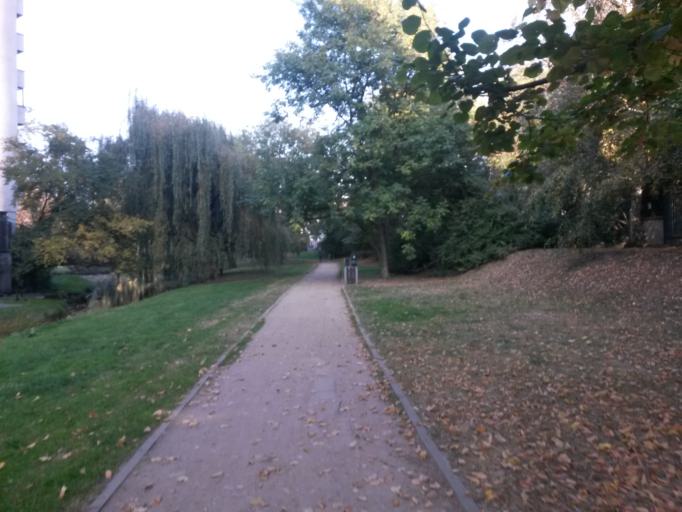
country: PL
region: Masovian Voivodeship
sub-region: Warszawa
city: Mokotow
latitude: 52.1970
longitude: 21.0412
